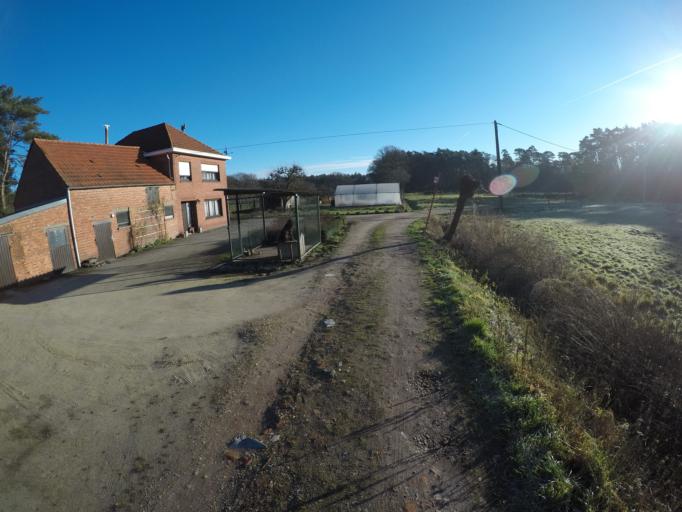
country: BE
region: Flanders
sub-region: Provincie Antwerpen
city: Schilde
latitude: 51.2409
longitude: 4.6255
